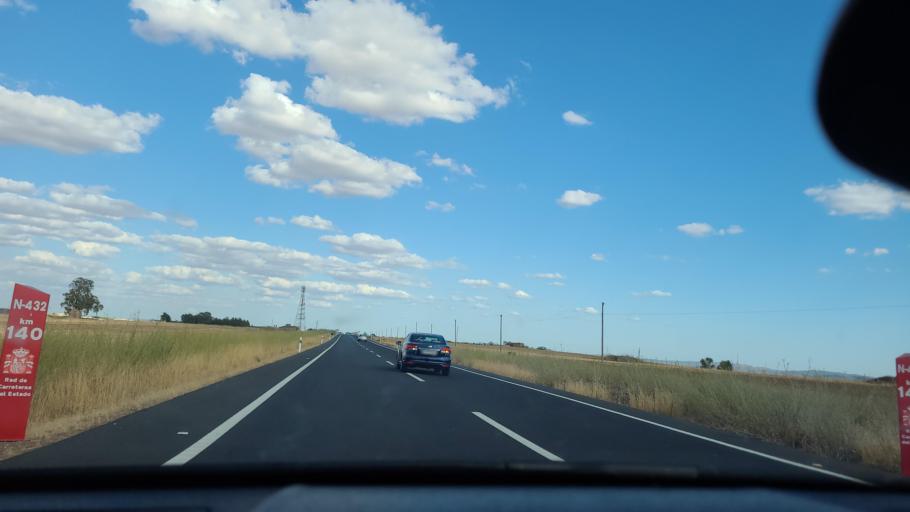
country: ES
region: Extremadura
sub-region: Provincia de Badajoz
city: Azuaga
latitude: 38.2616
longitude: -5.7281
